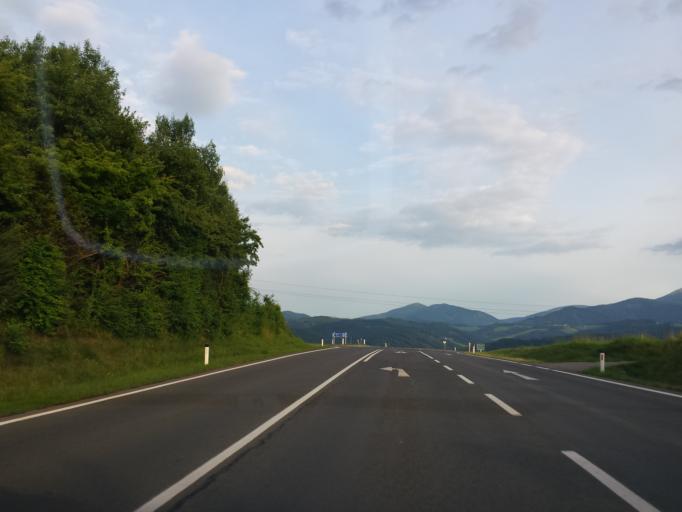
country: AT
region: Styria
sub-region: Politischer Bezirk Murtal
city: Spielberg bei Knittelfeld
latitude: 47.2107
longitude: 14.7856
